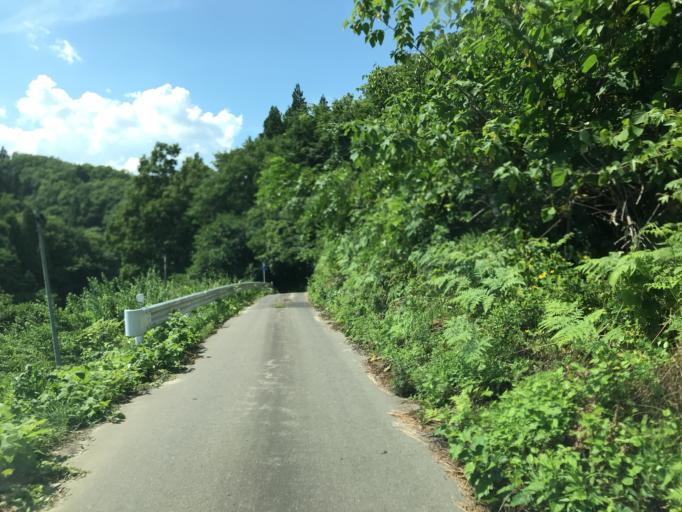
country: JP
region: Fukushima
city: Yanagawamachi-saiwaicho
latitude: 37.7806
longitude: 140.6551
